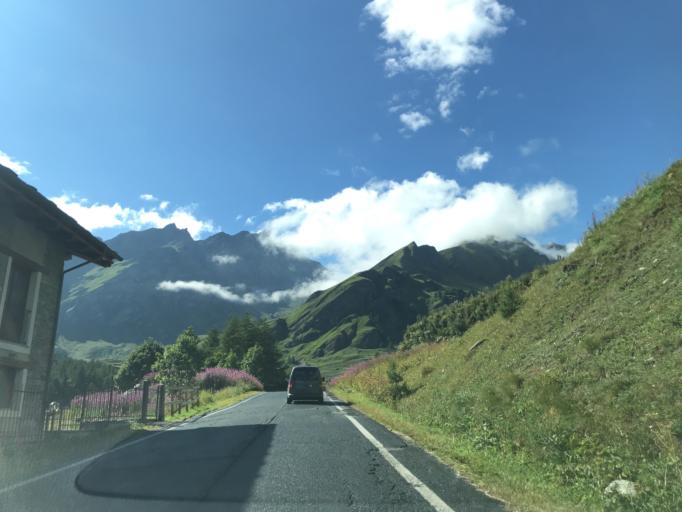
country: IT
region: Piedmont
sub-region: Provincia di Cuneo
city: Pontechianale
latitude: 44.6481
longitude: 6.9980
